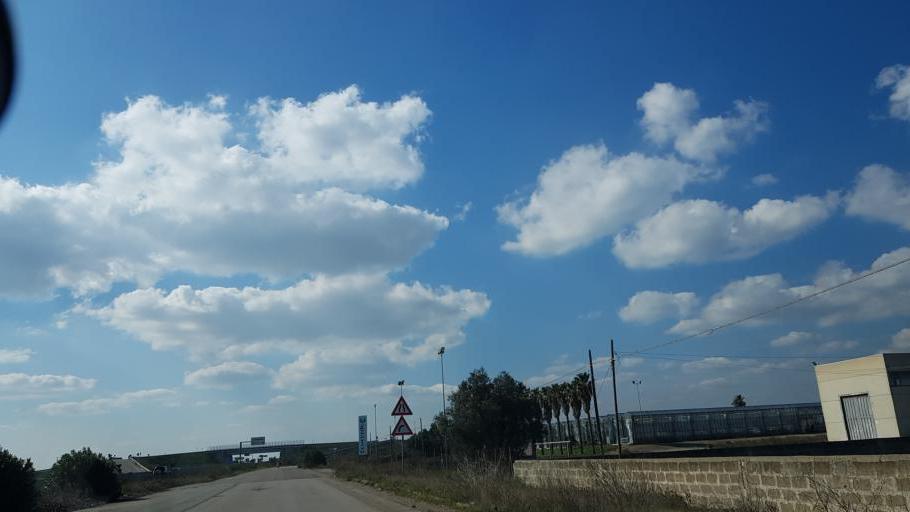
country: IT
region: Apulia
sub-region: Provincia di Brindisi
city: Mesagne
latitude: 40.5935
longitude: 17.8636
